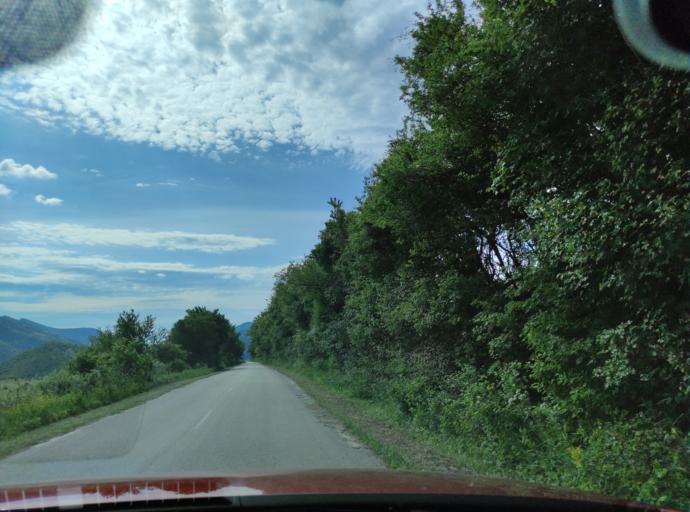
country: BG
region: Vidin
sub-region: Obshtina Belogradchik
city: Belogradchik
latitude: 43.5092
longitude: 22.7479
